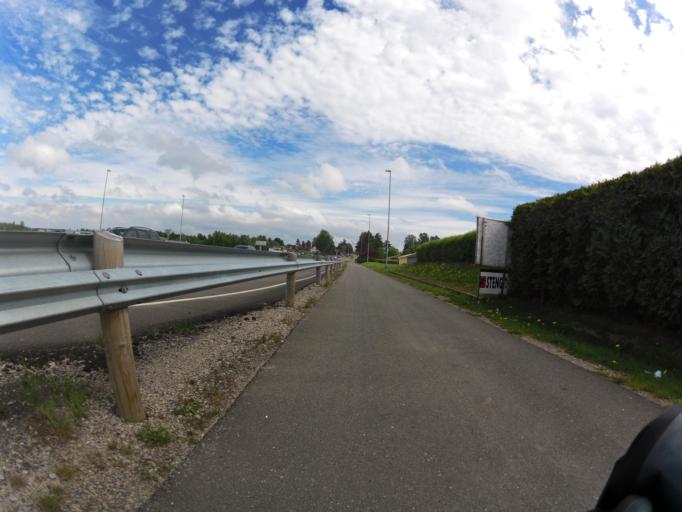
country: NO
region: Ostfold
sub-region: Rade
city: Karlshus
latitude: 59.3544
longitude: 10.8517
